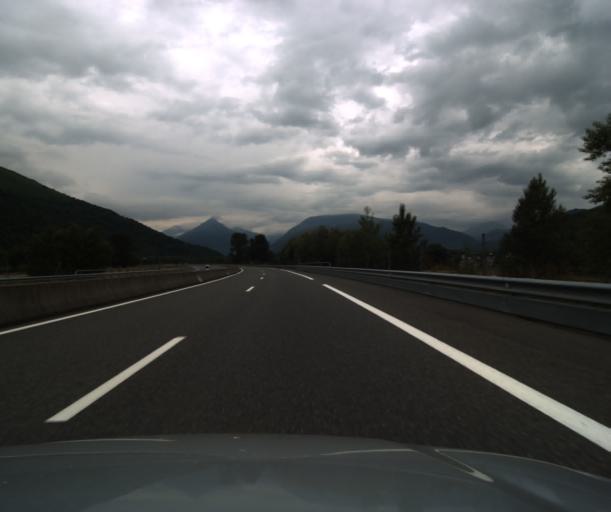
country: FR
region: Midi-Pyrenees
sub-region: Departement des Hautes-Pyrenees
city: Argeles-Gazost
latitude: 43.0406
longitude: -0.0648
